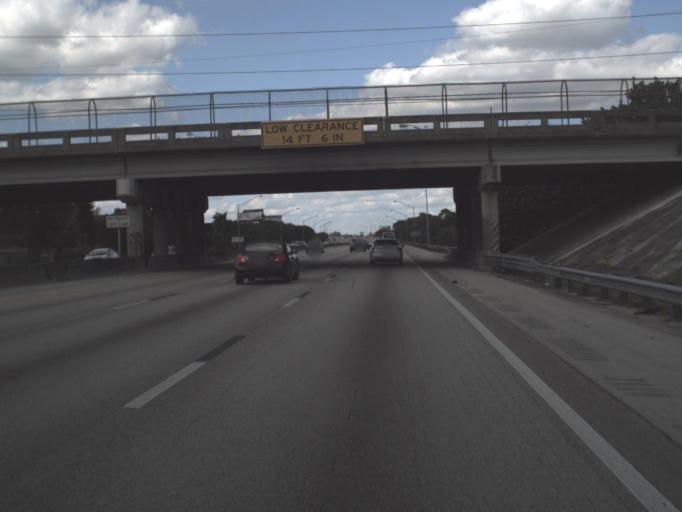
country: US
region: Florida
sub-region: Broward County
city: Pembroke Pines
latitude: 26.0317
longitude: -80.2133
